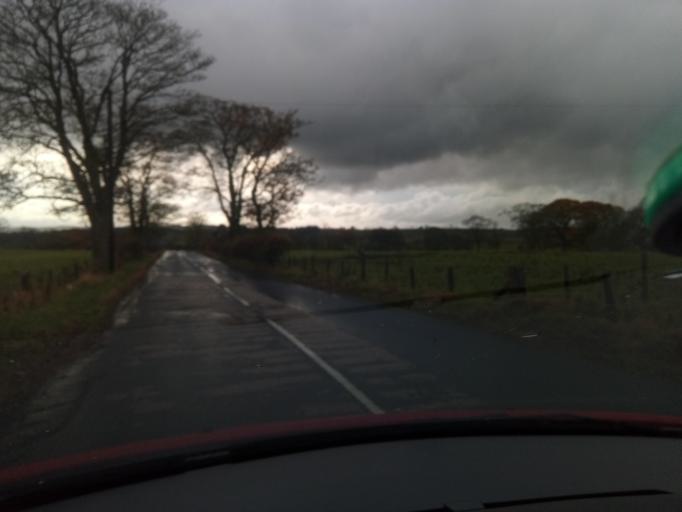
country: GB
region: England
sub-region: Northumberland
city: Birtley
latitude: 55.1179
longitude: -2.2414
